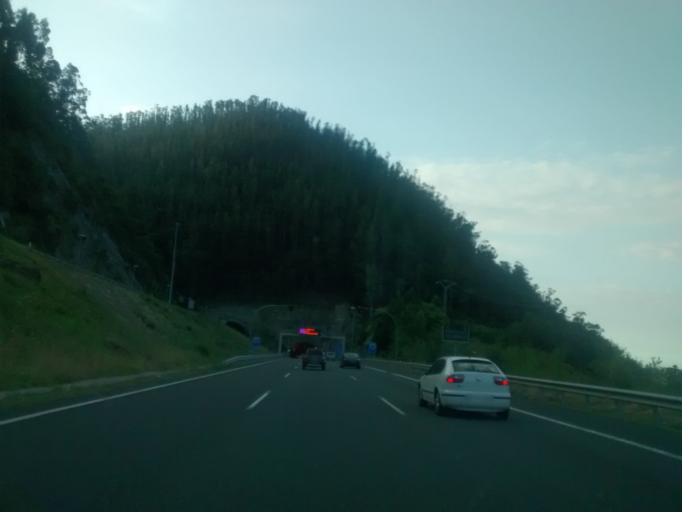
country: ES
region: Cantabria
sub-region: Provincia de Cantabria
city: Cartes
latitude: 43.2980
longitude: -4.0771
